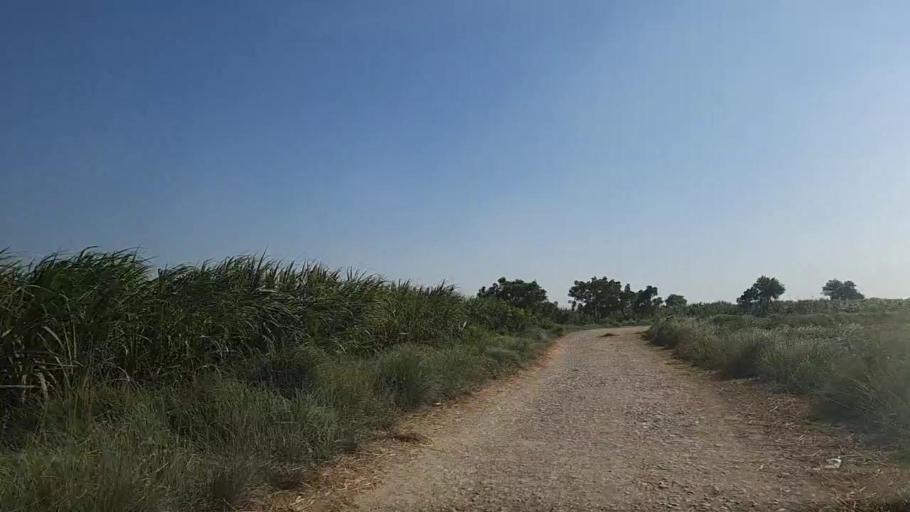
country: PK
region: Sindh
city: Daro Mehar
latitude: 24.7688
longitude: 68.0694
